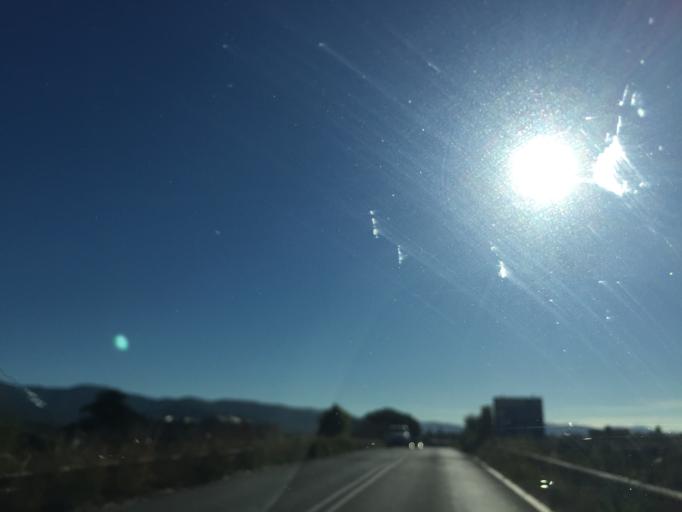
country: IT
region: Tuscany
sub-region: Provincia di Pistoia
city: Pistoia
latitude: 43.9320
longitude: 10.8930
